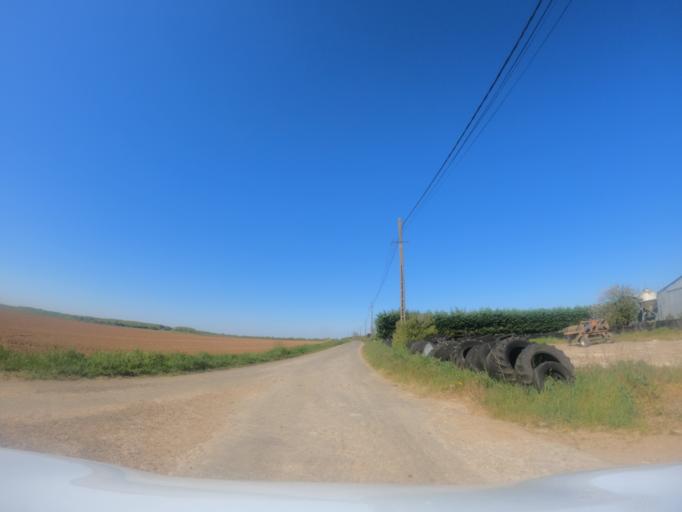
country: FR
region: Pays de la Loire
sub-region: Departement de la Vendee
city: Fontenay-le-Comte
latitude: 46.4282
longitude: -0.8152
